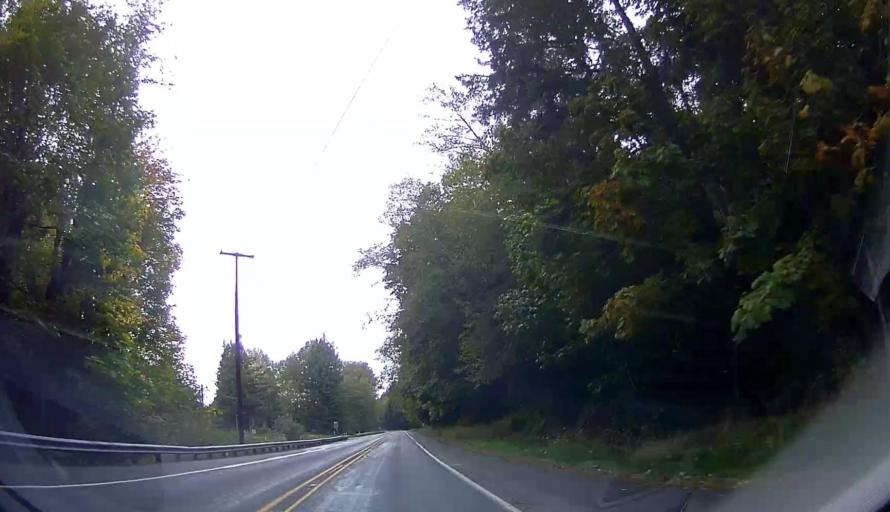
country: US
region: Washington
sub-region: Skagit County
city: Sedro-Woolley
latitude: 48.5250
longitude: -122.1195
